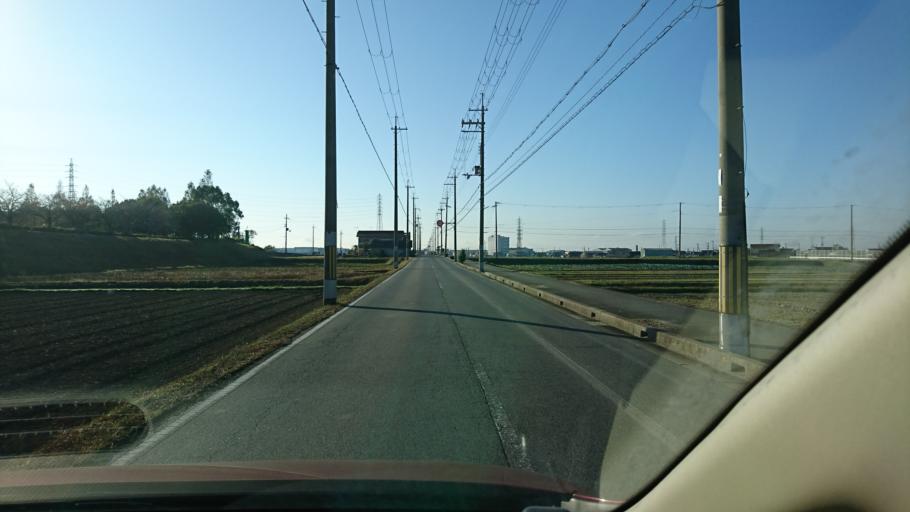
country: JP
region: Hyogo
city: Miki
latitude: 34.7401
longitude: 134.9218
